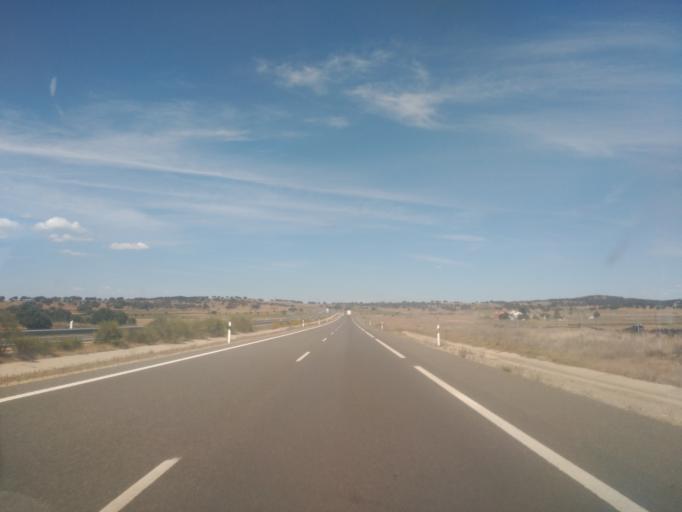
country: ES
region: Castille and Leon
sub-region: Provincia de Salamanca
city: Pizarral
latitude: 40.6082
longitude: -5.6435
